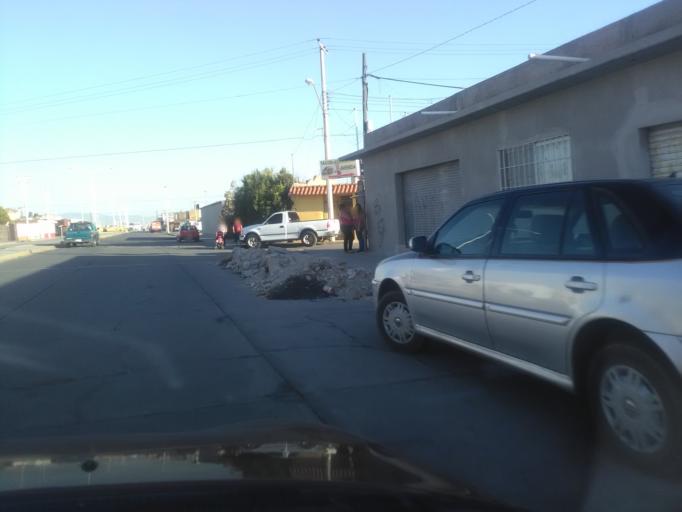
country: MX
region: Durango
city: Victoria de Durango
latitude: 24.0580
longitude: -104.5912
